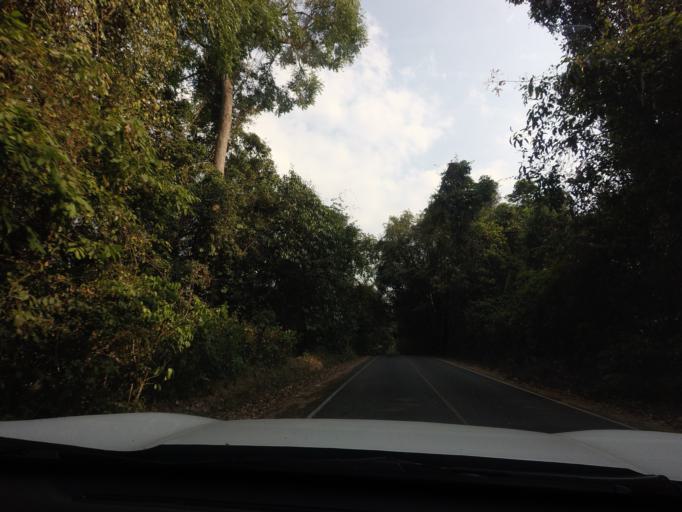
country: TH
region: Nakhon Ratchasima
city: Pak Chong
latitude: 14.4349
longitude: 101.4112
